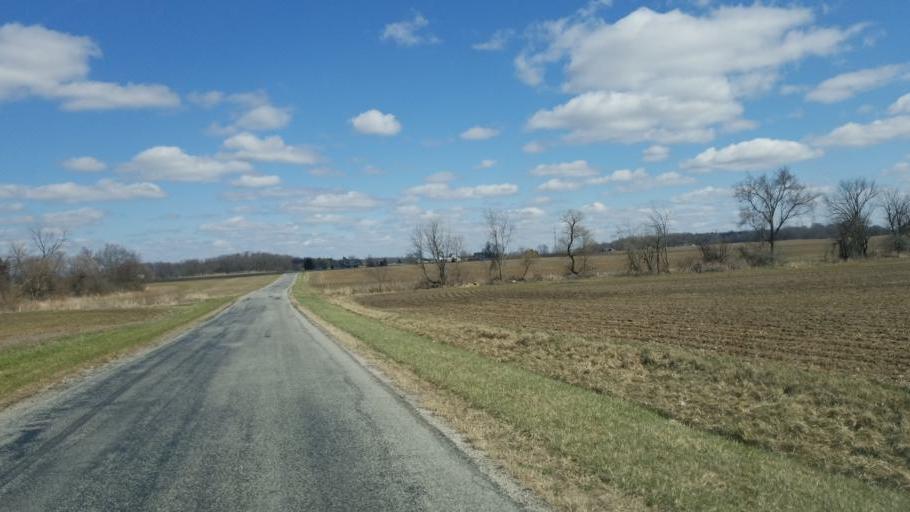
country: US
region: Ohio
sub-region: Richland County
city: Shelby
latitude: 40.8866
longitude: -82.6115
